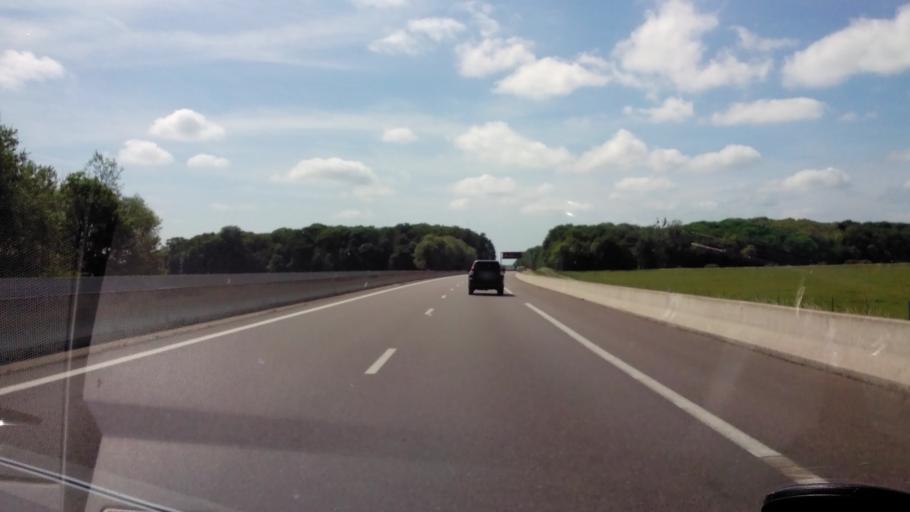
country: FR
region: Lorraine
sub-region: Departement des Vosges
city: Chatenois
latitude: 48.3265
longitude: 5.8565
